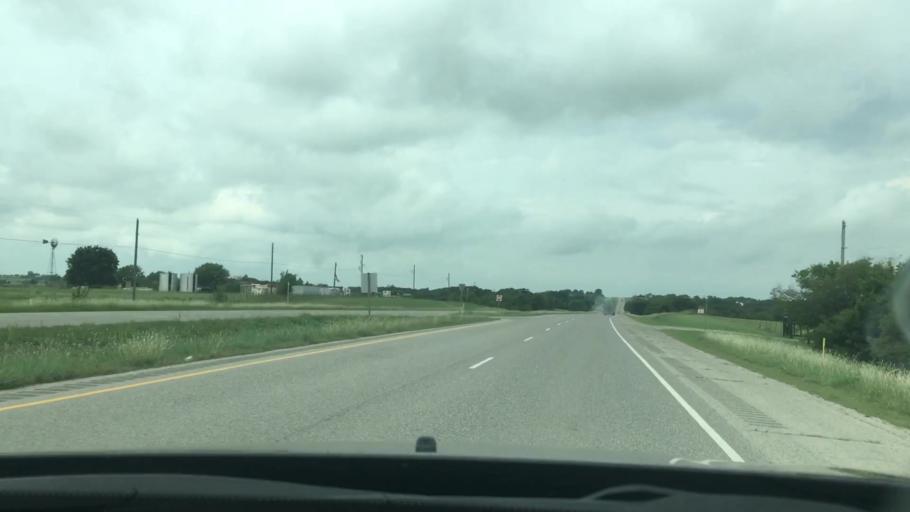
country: US
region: Oklahoma
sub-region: Carter County
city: Wilson
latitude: 34.1731
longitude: -97.4431
